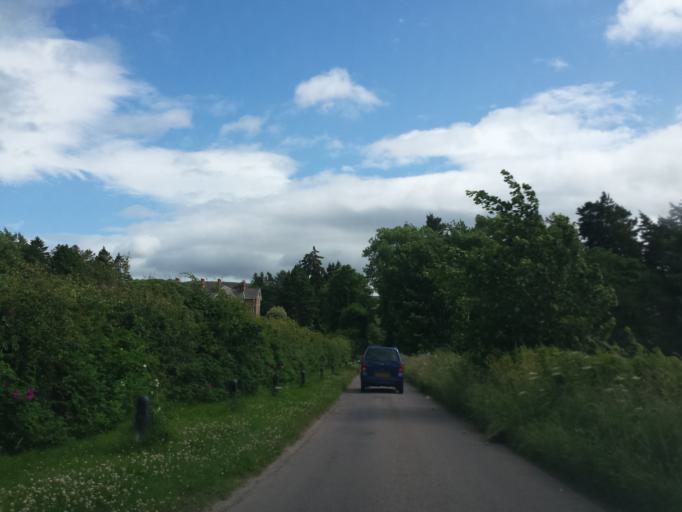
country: GB
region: Scotland
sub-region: Highland
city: Fortrose
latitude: 57.4765
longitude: -4.0704
